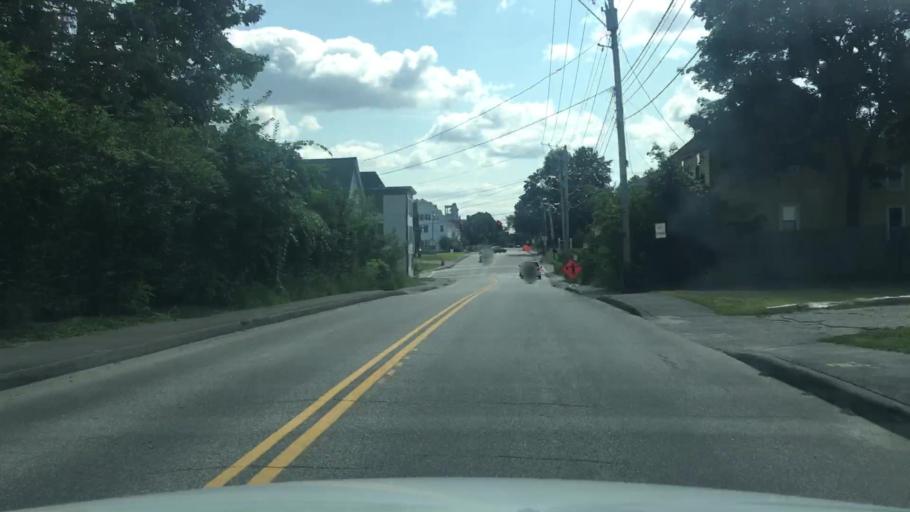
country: US
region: Maine
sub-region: Kennebec County
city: Augusta
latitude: 44.3185
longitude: -69.7761
